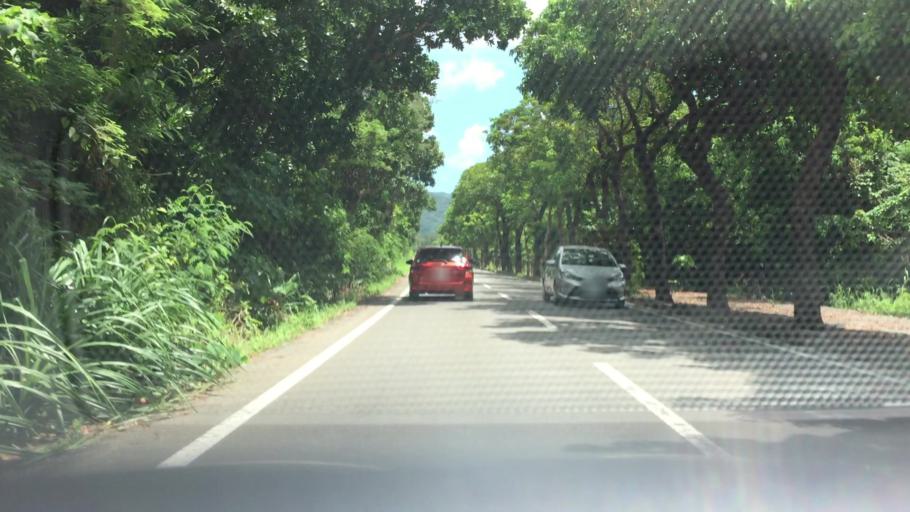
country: JP
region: Okinawa
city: Ishigaki
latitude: 24.3892
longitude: 124.1405
